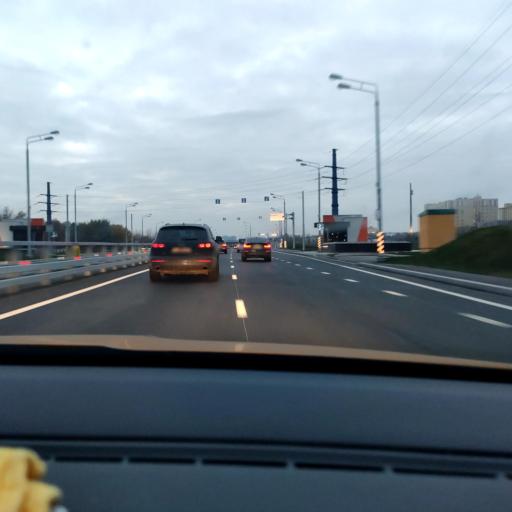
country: RU
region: Moscow
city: Vorob'yovo
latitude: 55.7330
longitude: 37.5296
